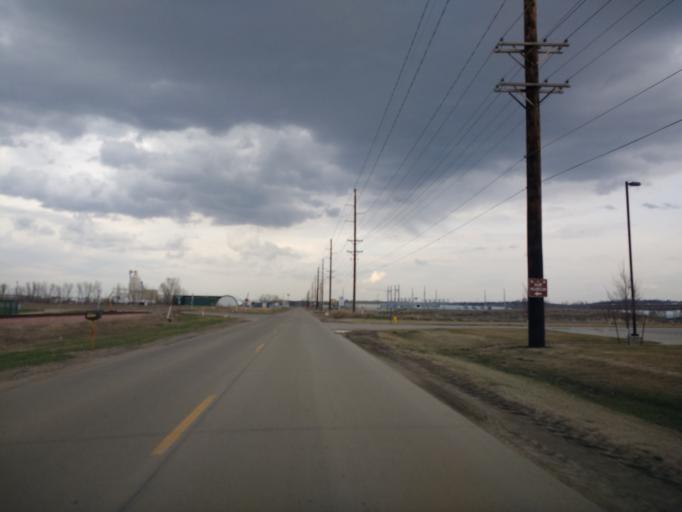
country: US
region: Iowa
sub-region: Woodbury County
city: Sergeant Bluff
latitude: 42.4140
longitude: -96.3700
